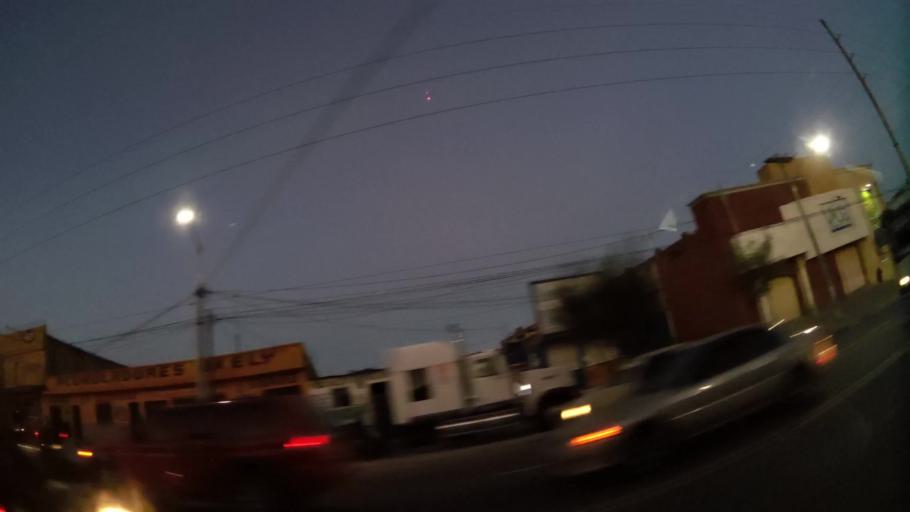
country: GT
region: Guatemala
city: Villa Nueva
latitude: 14.5115
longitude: -90.5725
